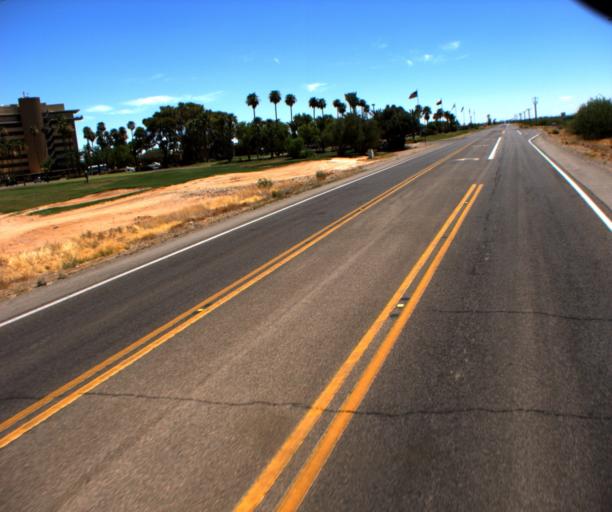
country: US
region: Arizona
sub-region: Pinal County
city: Casa Grande
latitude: 32.8794
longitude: -111.8499
